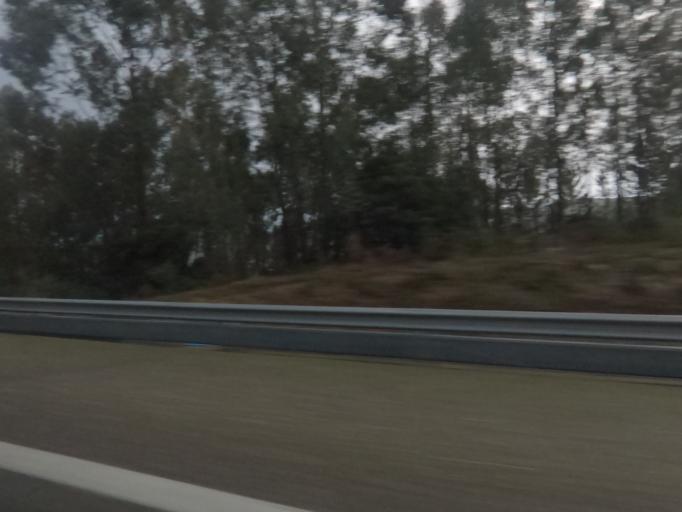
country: PT
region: Viana do Castelo
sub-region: Ponte de Lima
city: Ponte de Lima
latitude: 41.8196
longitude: -8.6001
